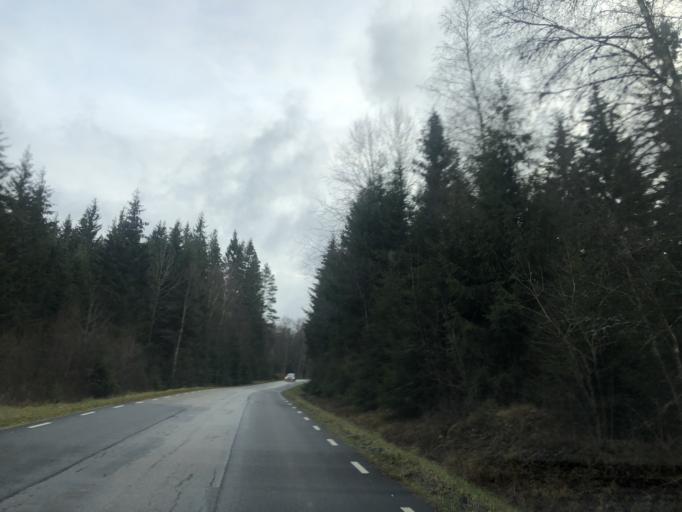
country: SE
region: Vaestra Goetaland
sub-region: Boras Kommun
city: Dalsjofors
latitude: 57.8145
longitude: 13.1985
